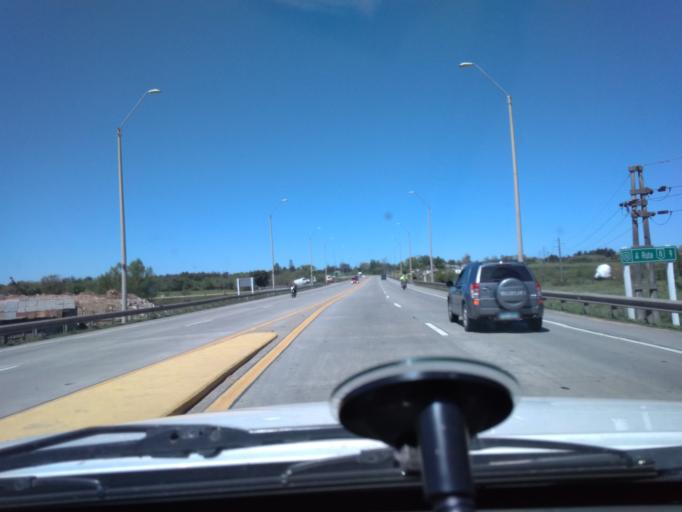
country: UY
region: Canelones
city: La Paz
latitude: -34.7957
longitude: -56.1631
